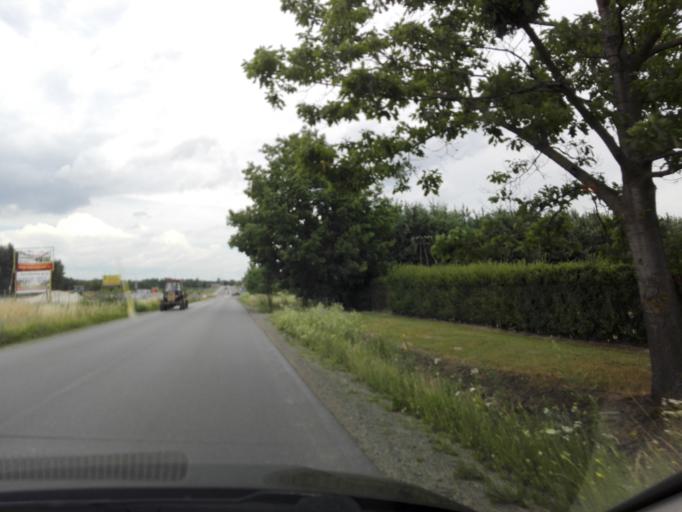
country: PL
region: Lublin Voivodeship
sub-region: Powiat pulawski
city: Kurow
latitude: 51.4008
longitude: 22.2007
